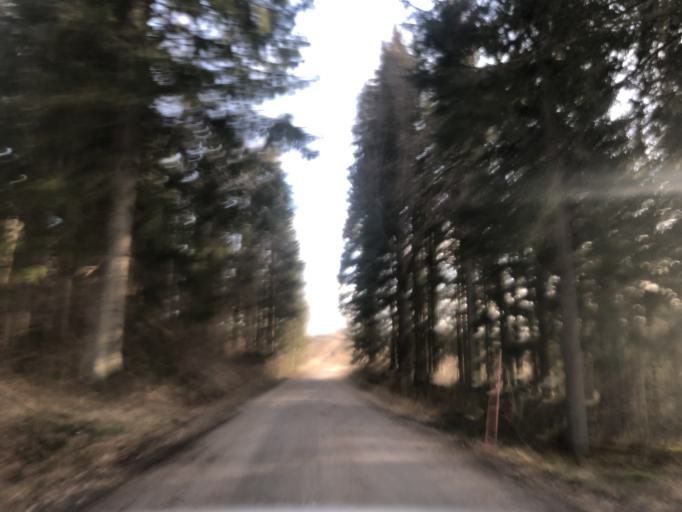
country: SE
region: Vaestra Goetaland
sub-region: Ulricehamns Kommun
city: Ulricehamn
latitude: 57.8167
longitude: 13.3600
